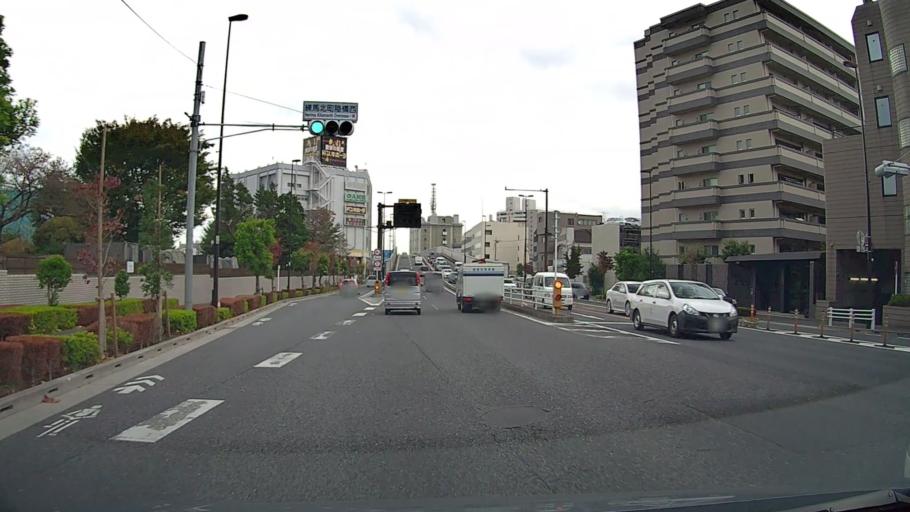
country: JP
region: Saitama
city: Wako
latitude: 35.7627
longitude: 139.6619
